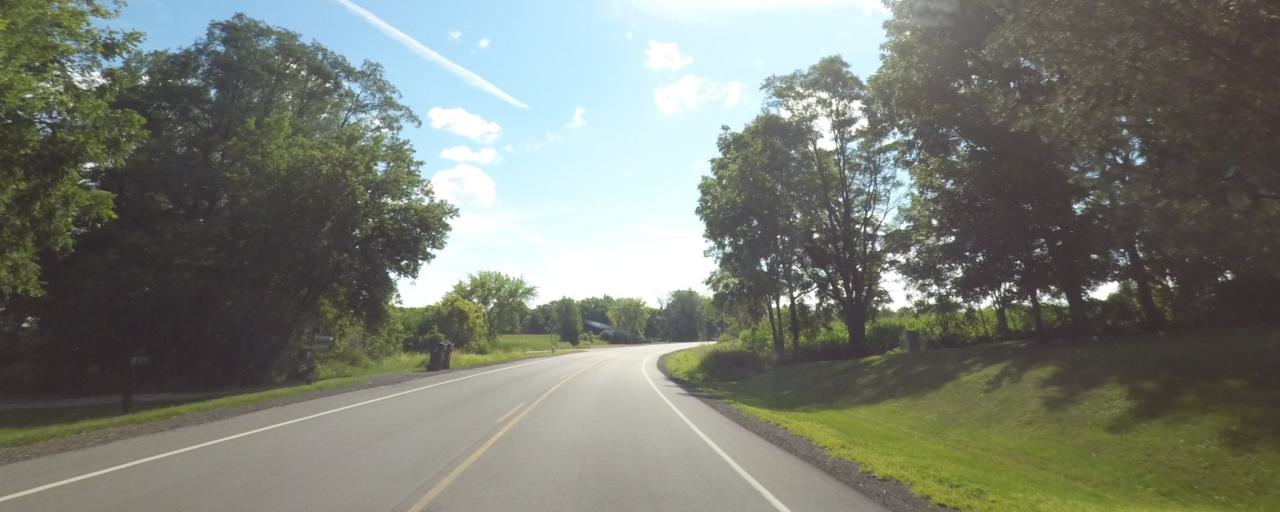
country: US
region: Wisconsin
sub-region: Waukesha County
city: Oconomowoc
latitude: 43.0762
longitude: -88.5616
